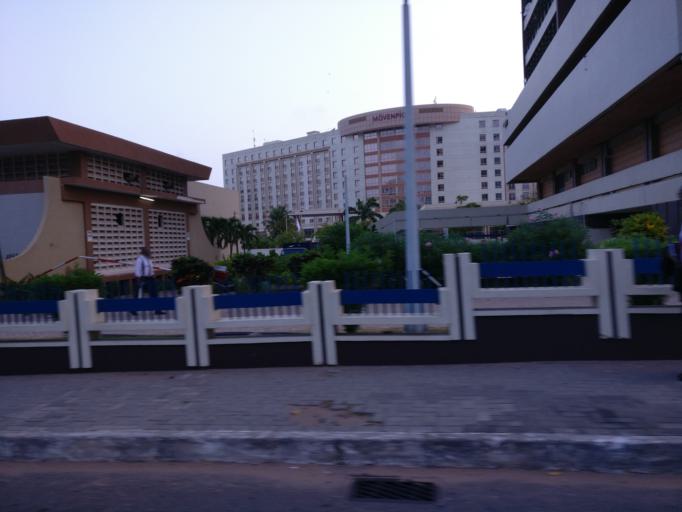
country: GH
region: Greater Accra
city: Accra
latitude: 5.5557
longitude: -0.2017
